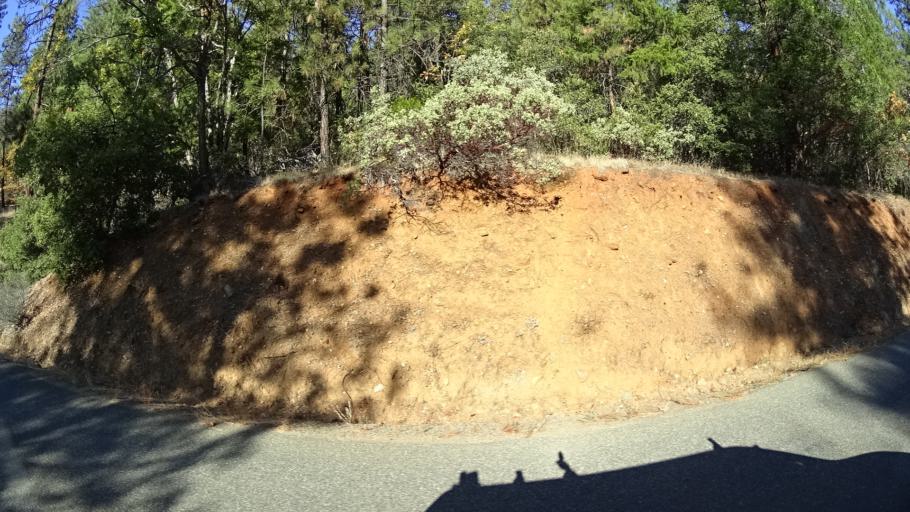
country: US
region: California
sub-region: Siskiyou County
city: Yreka
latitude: 41.7330
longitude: -123.0078
